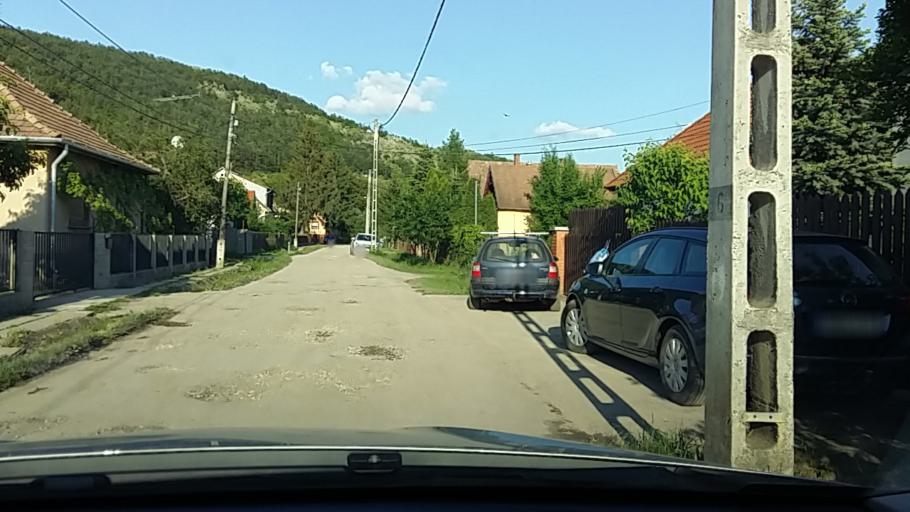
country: HU
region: Pest
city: Kosd
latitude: 47.8064
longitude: 19.2522
